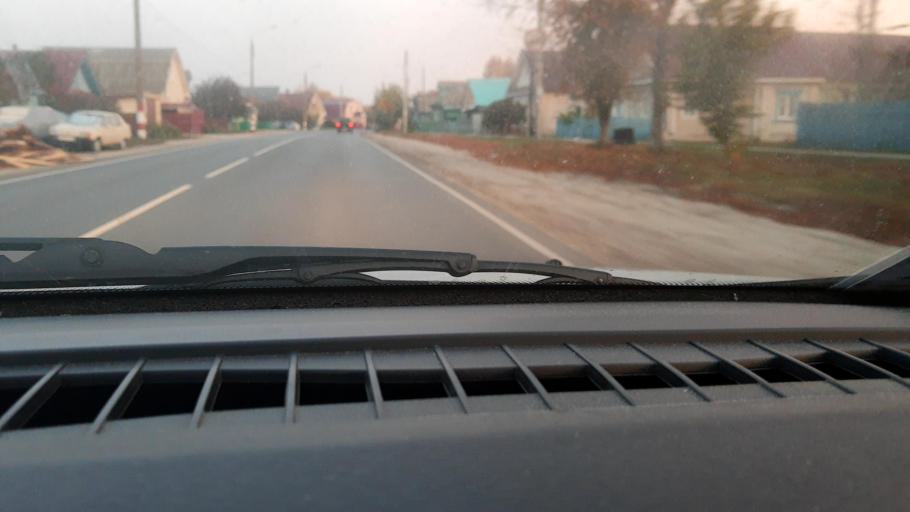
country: RU
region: Nizjnij Novgorod
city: Neklyudovo
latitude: 56.3794
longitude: 44.0164
